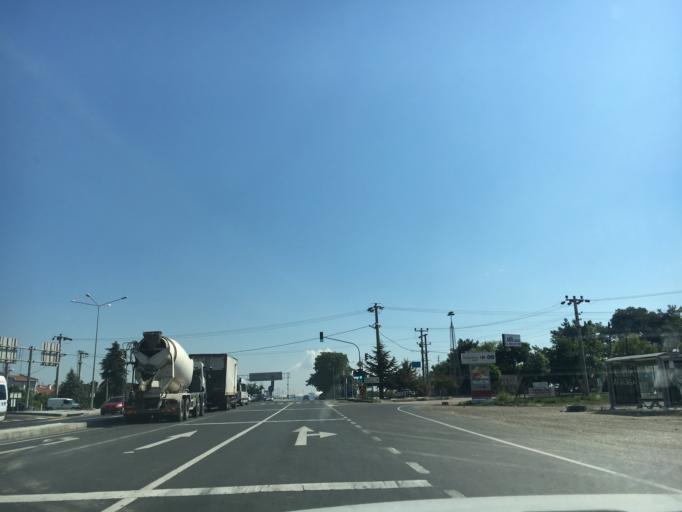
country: TR
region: Tekirdag
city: Marmara Ereglisi
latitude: 40.9771
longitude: 27.9529
